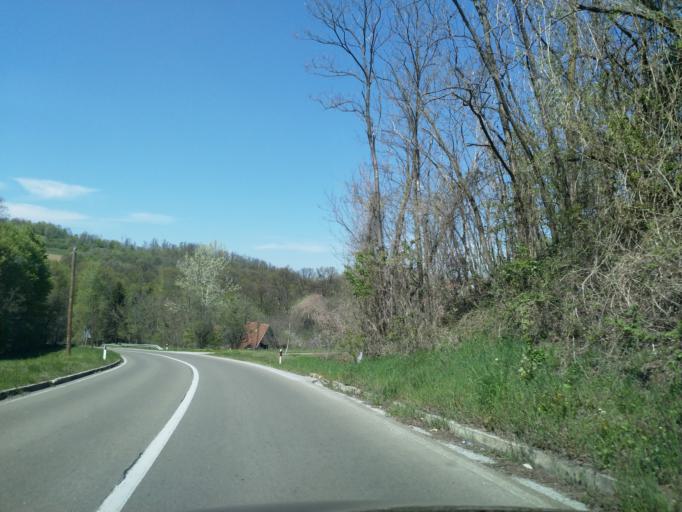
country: RS
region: Central Serbia
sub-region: Belgrade
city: Lazarevac
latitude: 44.3552
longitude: 20.3536
